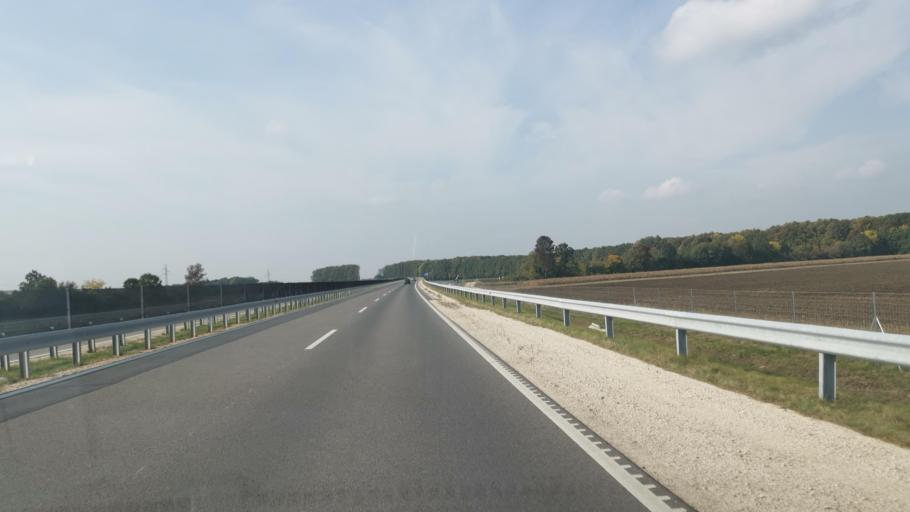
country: HU
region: Gyor-Moson-Sopron
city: Mihalyi
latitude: 47.5649
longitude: 17.1112
